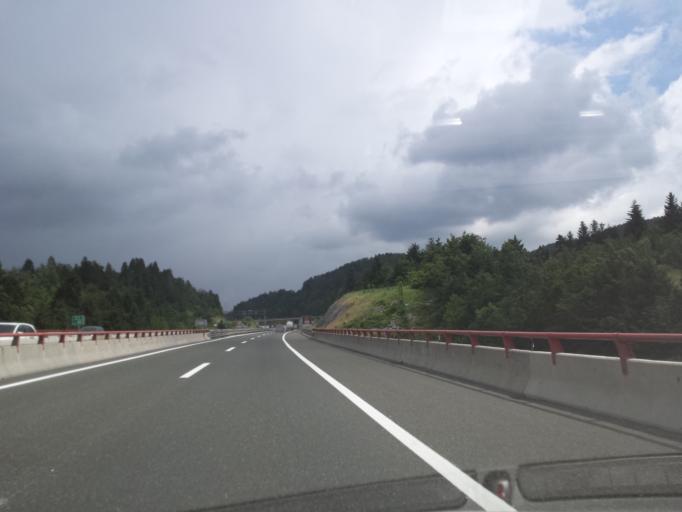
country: HR
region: Primorsko-Goranska
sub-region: Grad Delnice
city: Delnice
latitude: 45.3590
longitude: 14.7639
